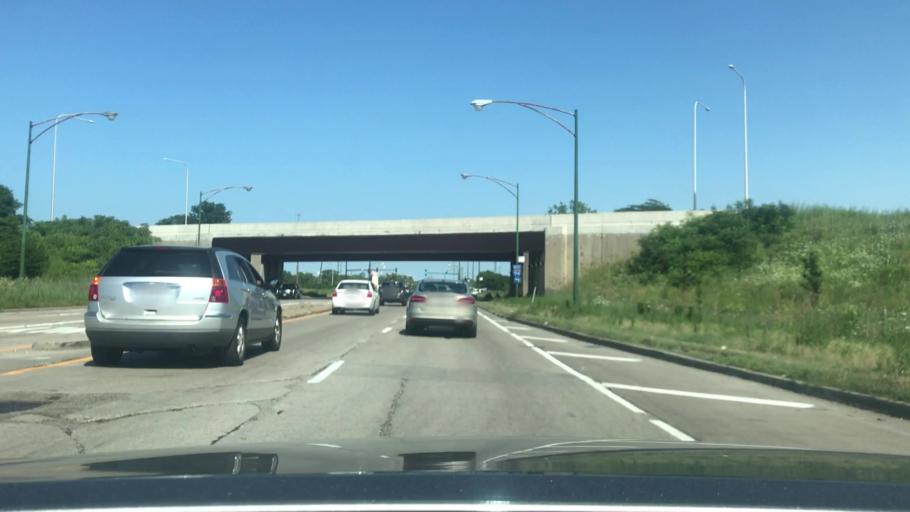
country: US
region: Illinois
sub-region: Cook County
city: Dolton
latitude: 41.7077
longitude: -87.5871
